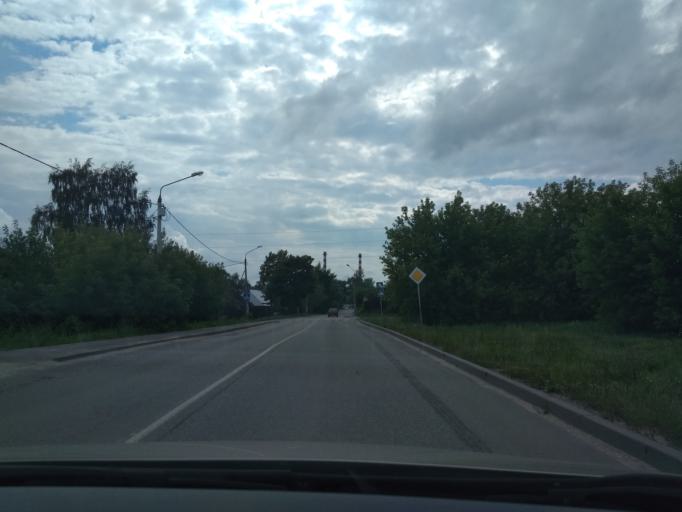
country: RU
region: Moskovskaya
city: Orekhovo-Zuyevo
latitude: 55.8024
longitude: 38.9519
